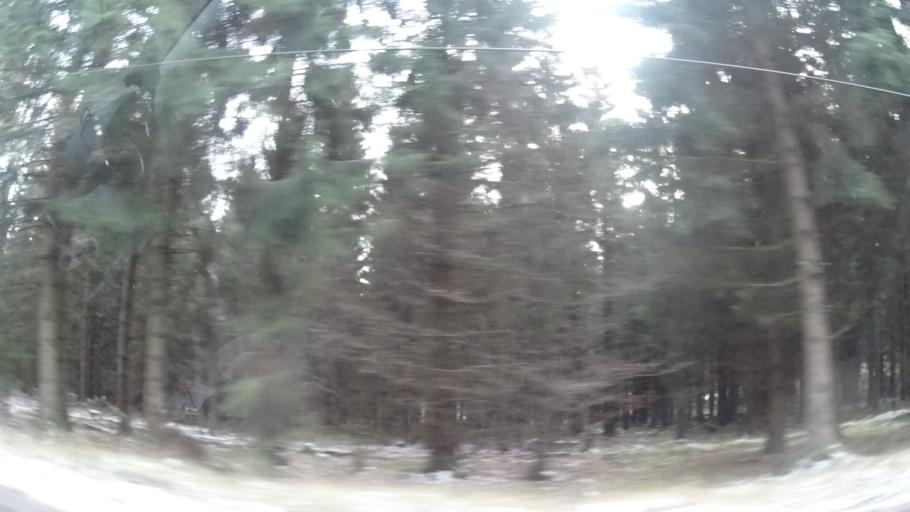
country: DE
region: Thuringia
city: Tabarz
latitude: 50.8370
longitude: 10.5174
